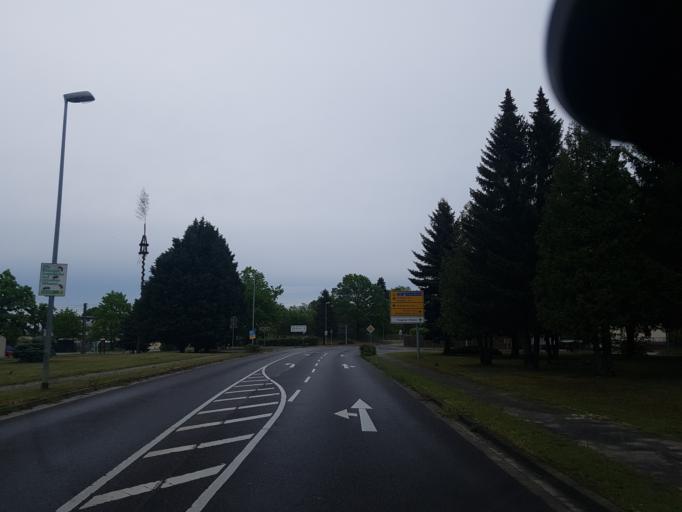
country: DE
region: Brandenburg
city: Neupetershain
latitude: 51.6239
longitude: 14.1602
